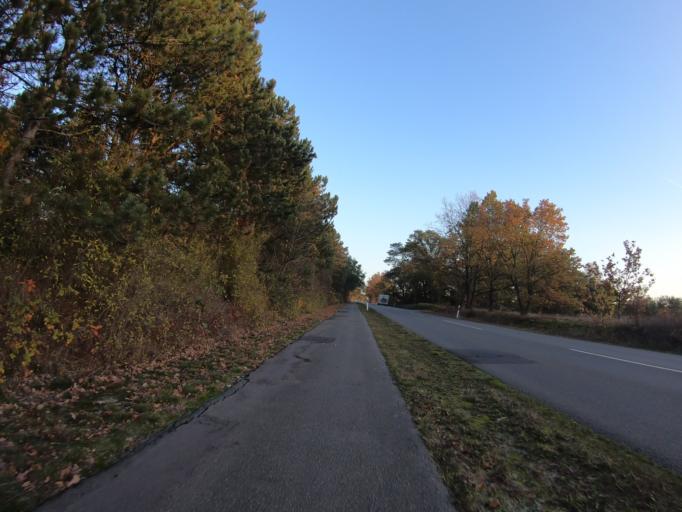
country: DE
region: Lower Saxony
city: Wagenhoff
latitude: 52.5037
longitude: 10.4975
